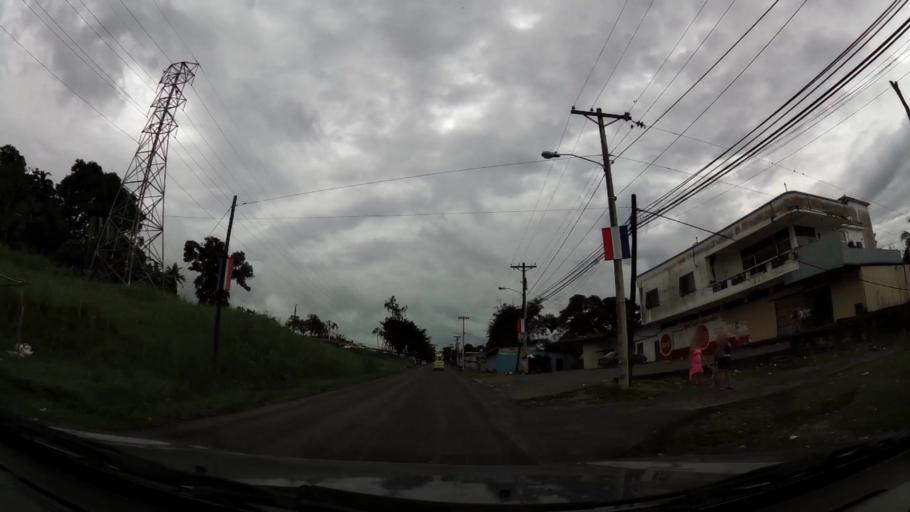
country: PA
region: Panama
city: Chilibre
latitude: 9.1729
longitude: -79.6108
